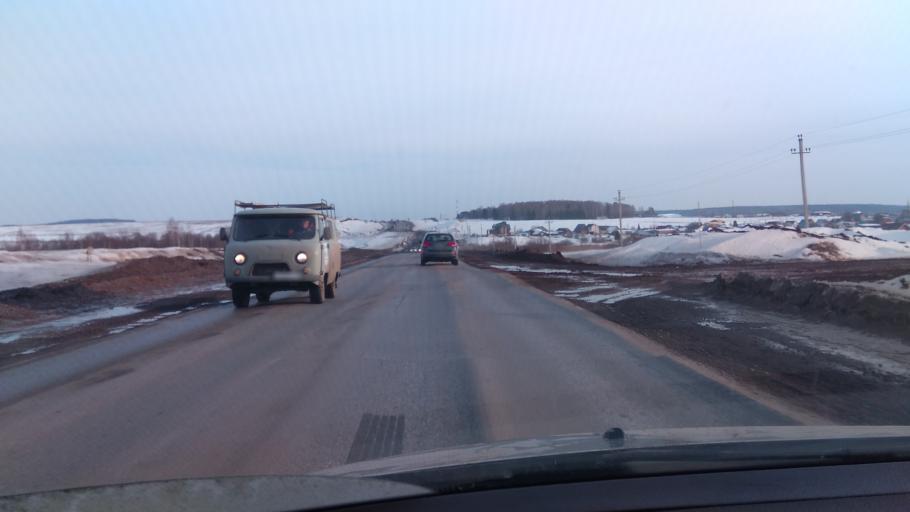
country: RU
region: Perm
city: Lobanovo
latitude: 57.8079
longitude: 56.3194
